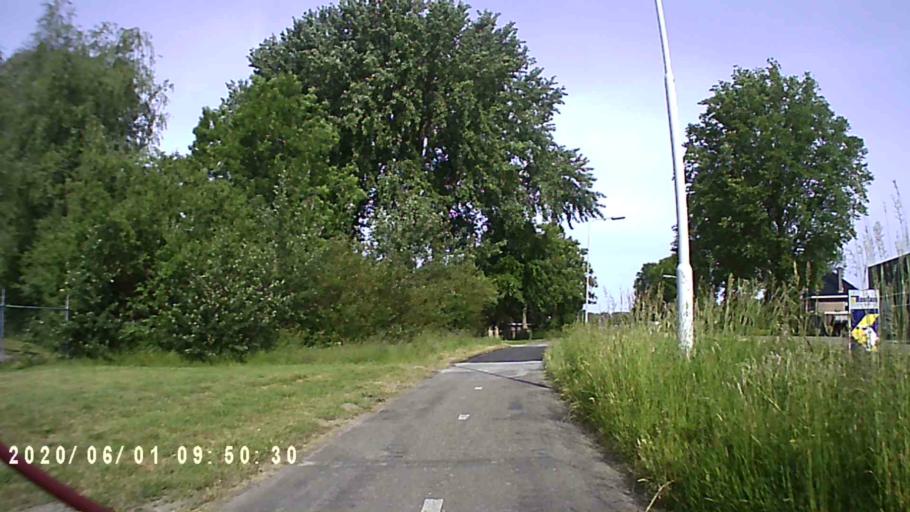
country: NL
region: Friesland
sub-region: Menameradiel
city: Berltsum
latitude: 53.2420
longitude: 5.6621
